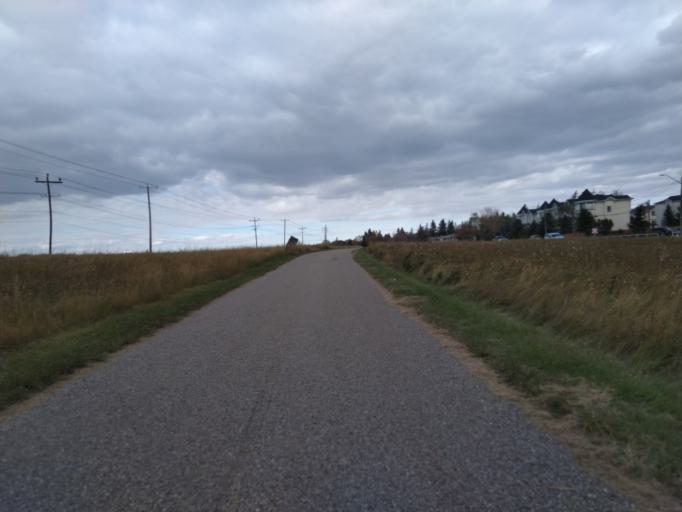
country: CA
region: Alberta
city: Calgary
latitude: 51.0283
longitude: -113.9959
